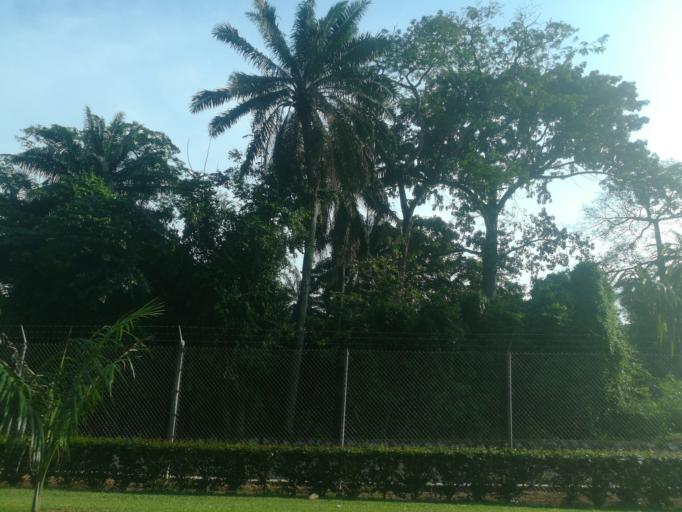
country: NG
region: Oyo
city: Moniya
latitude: 7.4998
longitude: 3.9120
